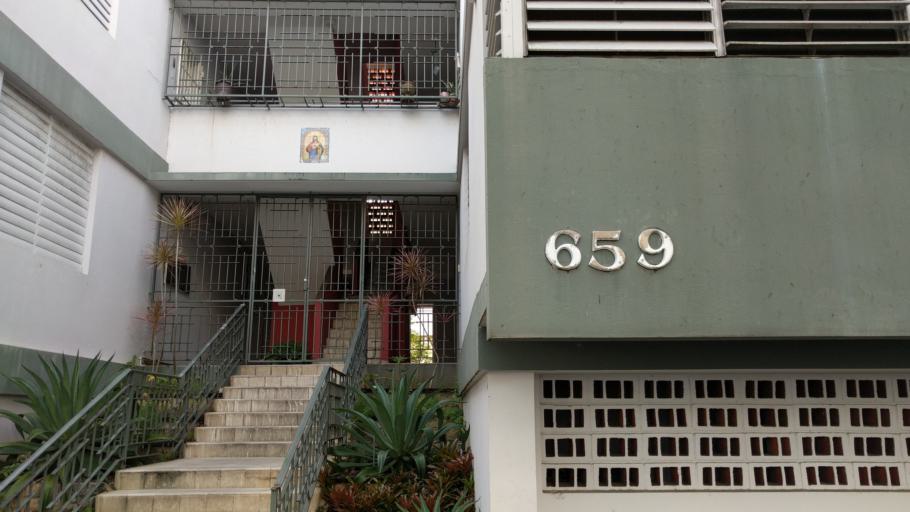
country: PR
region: San Juan
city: San Juan
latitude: 18.4542
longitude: -66.0852
